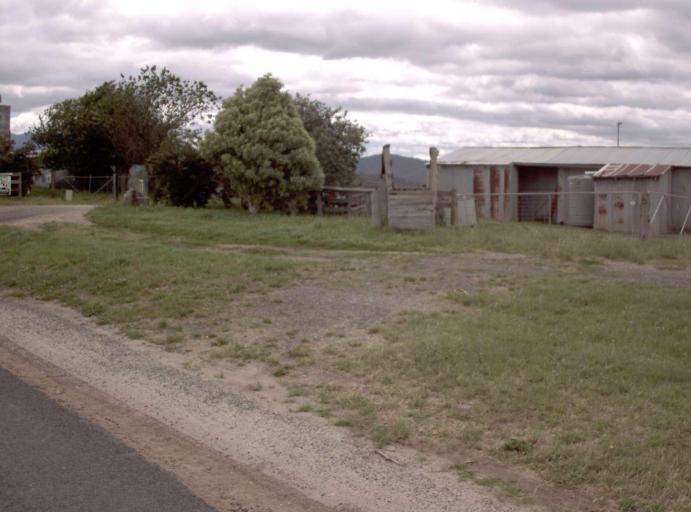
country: AU
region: Victoria
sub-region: Latrobe
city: Moe
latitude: -37.9975
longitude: 146.1463
